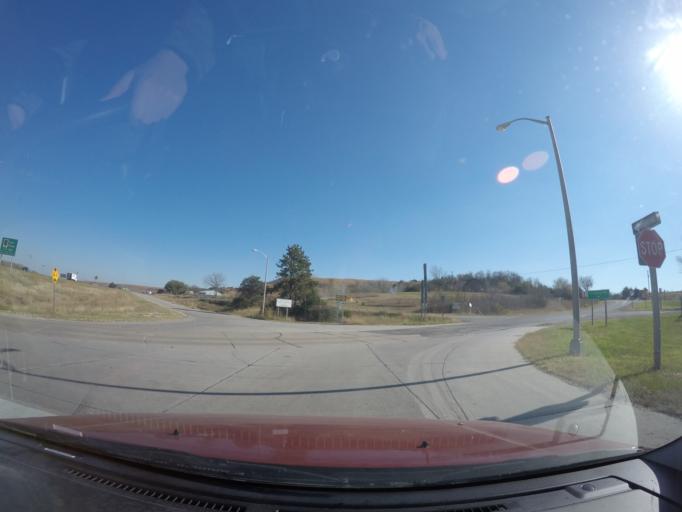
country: US
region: Kansas
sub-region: Geary County
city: Grandview Plaza
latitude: 39.0299
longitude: -96.7837
